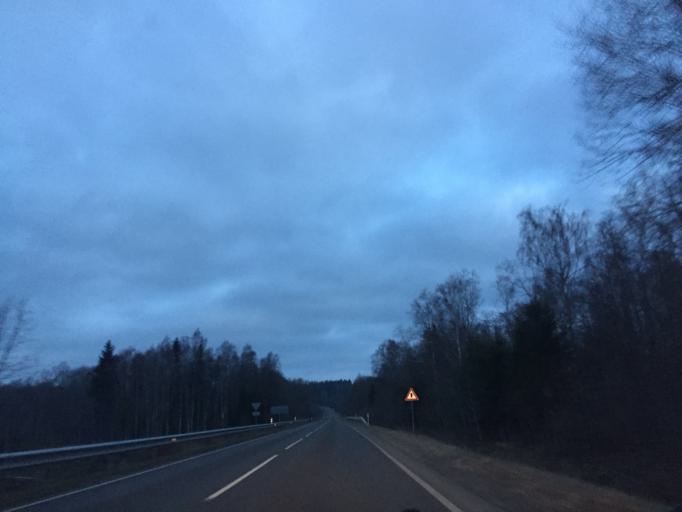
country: LV
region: Amatas Novads
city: Drabesi
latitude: 57.0658
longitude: 25.1793
